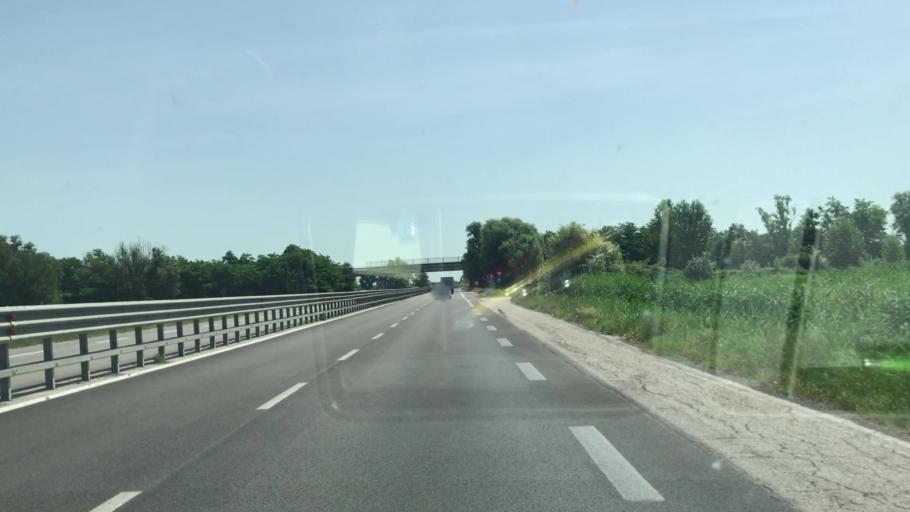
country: IT
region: Veneto
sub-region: Provincia di Rovigo
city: Fratta Polesine
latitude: 45.0234
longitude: 11.6207
